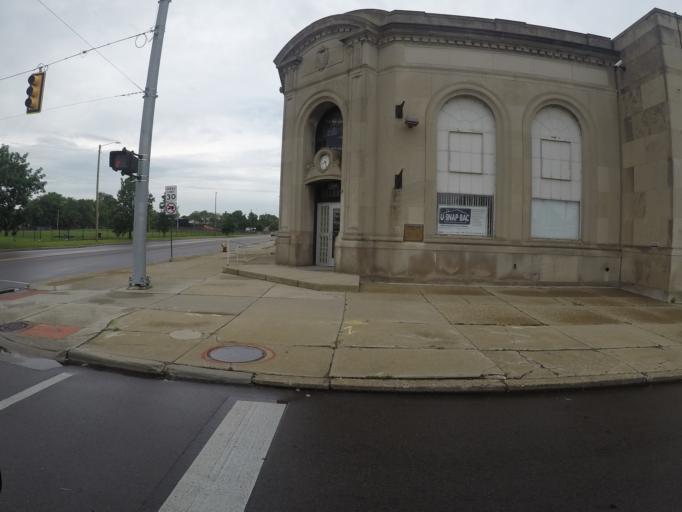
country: US
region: Michigan
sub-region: Wayne County
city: Grosse Pointe Park
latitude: 42.3973
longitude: -82.9544
